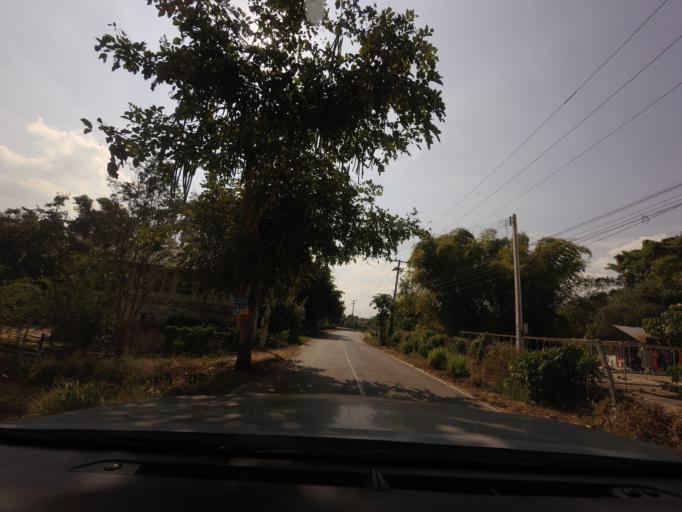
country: TH
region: Mae Hong Son
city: Wiang Nuea
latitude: 19.3883
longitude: 98.4412
